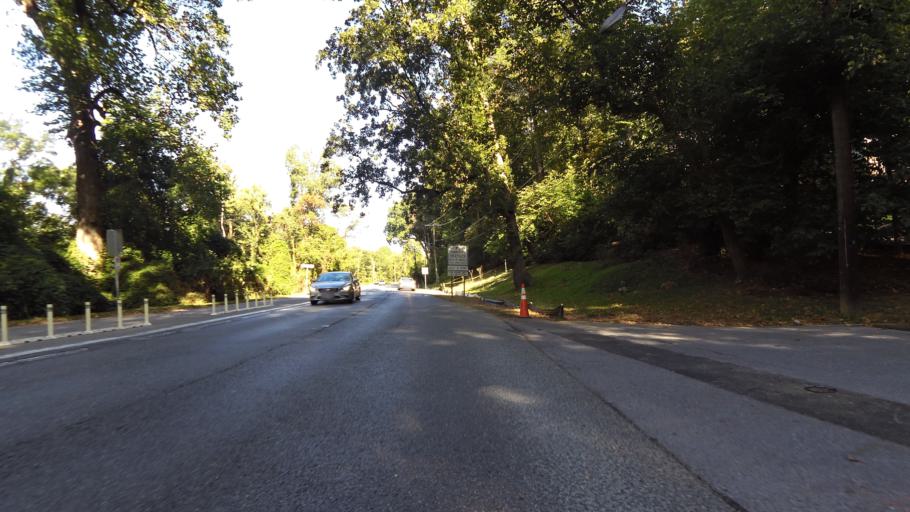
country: US
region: Maryland
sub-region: Montgomery County
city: Brookmont
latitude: 38.9609
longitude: -77.1330
